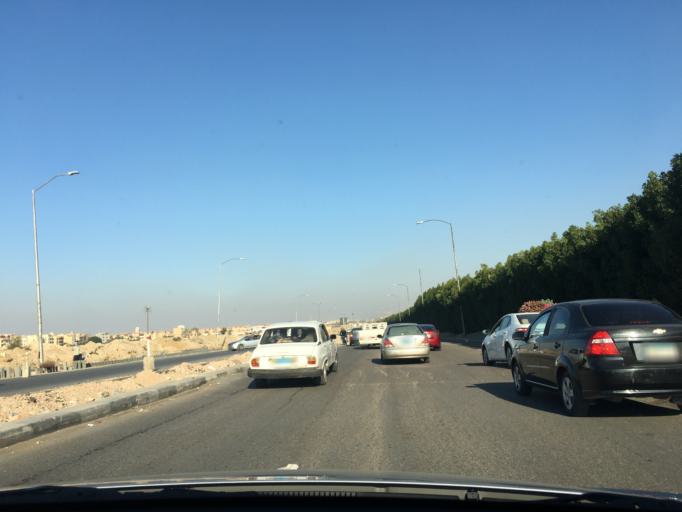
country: EG
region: Al Jizah
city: Madinat Sittah Uktubar
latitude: 29.9892
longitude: 30.9426
